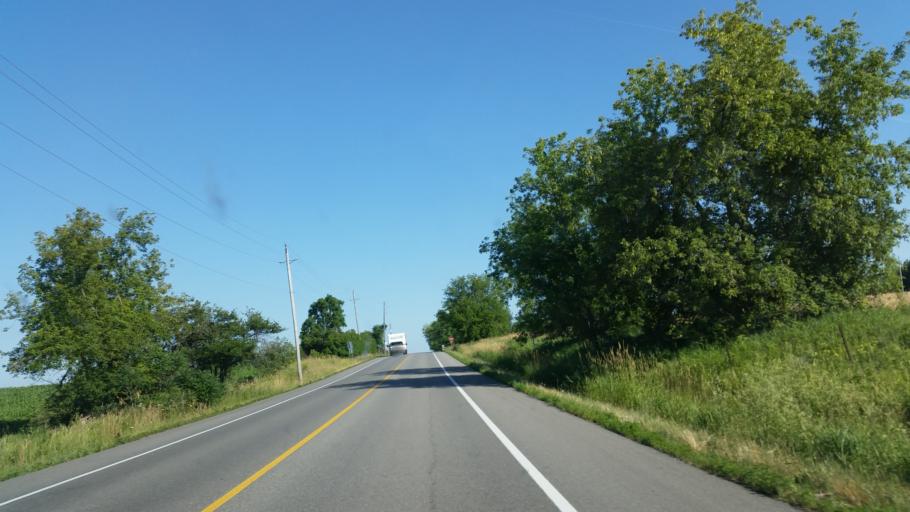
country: CA
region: Ontario
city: Bradford West Gwillimbury
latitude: 43.9580
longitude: -79.7745
